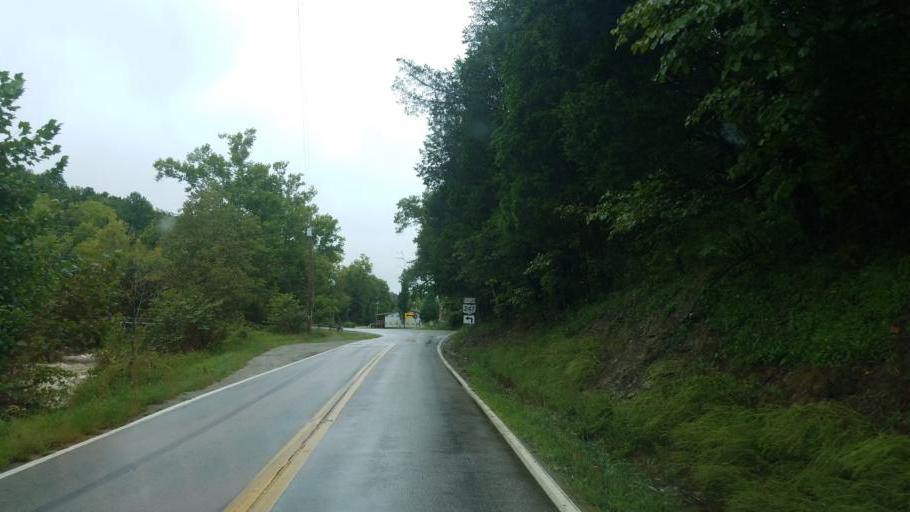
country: US
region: Ohio
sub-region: Adams County
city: West Union
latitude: 38.7474
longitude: -83.5176
